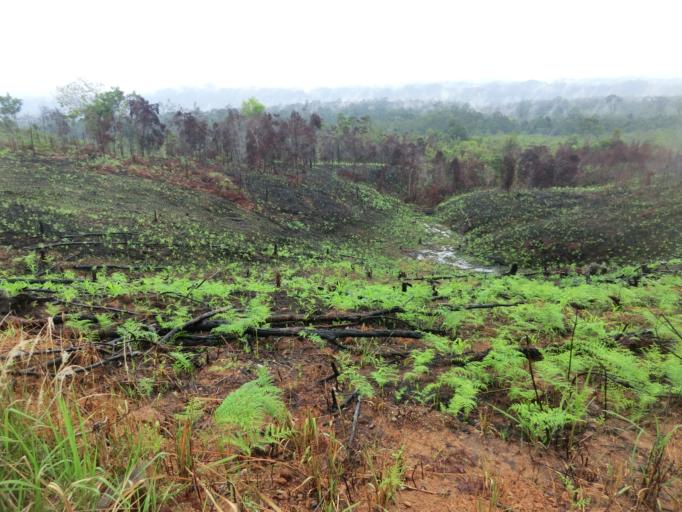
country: MY
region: Sarawak
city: Simanggang
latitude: 1.0989
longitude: 112.1670
